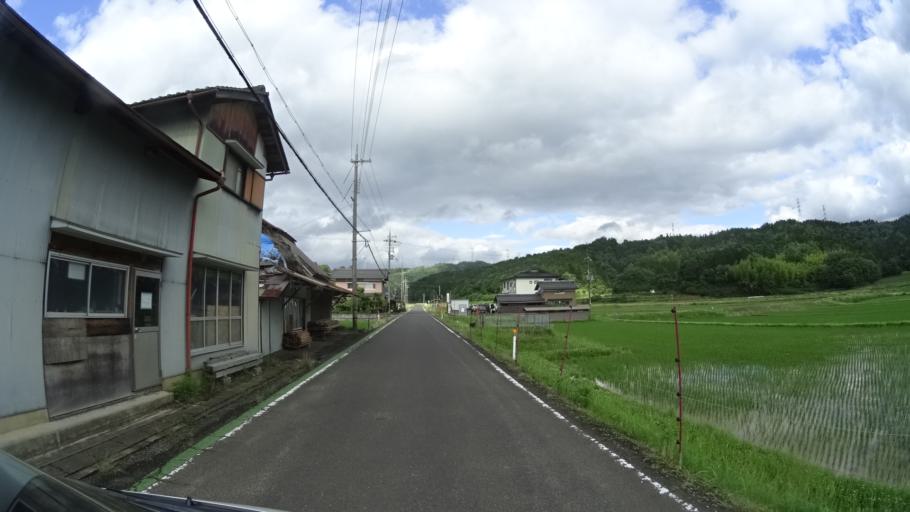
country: JP
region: Kyoto
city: Ayabe
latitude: 35.3658
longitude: 135.2584
